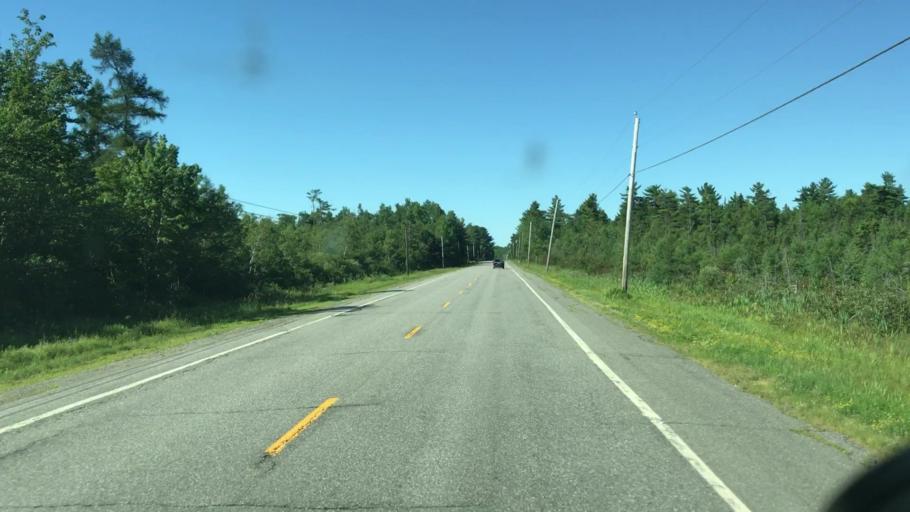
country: US
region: Maine
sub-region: Penobscot County
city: Howland
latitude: 45.2828
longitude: -68.6284
